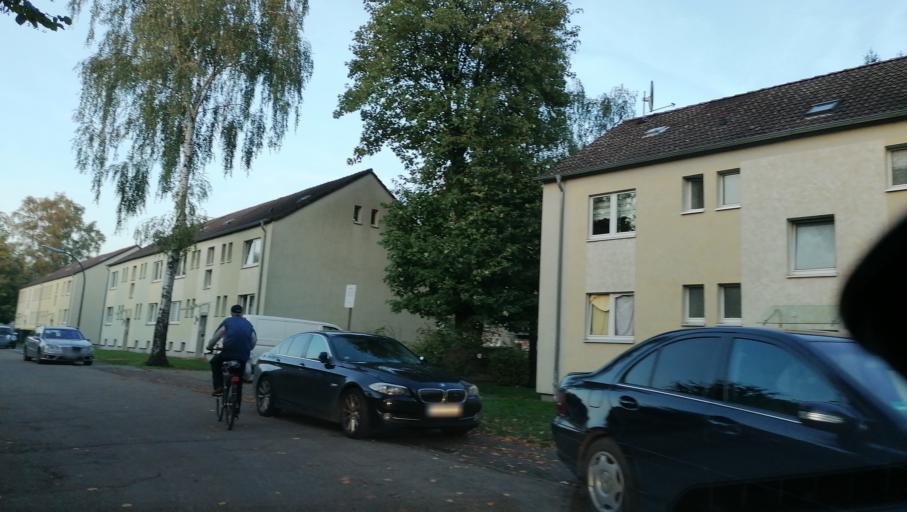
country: DE
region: North Rhine-Westphalia
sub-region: Regierungsbezirk Munster
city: Recklinghausen
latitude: 51.5708
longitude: 7.1846
